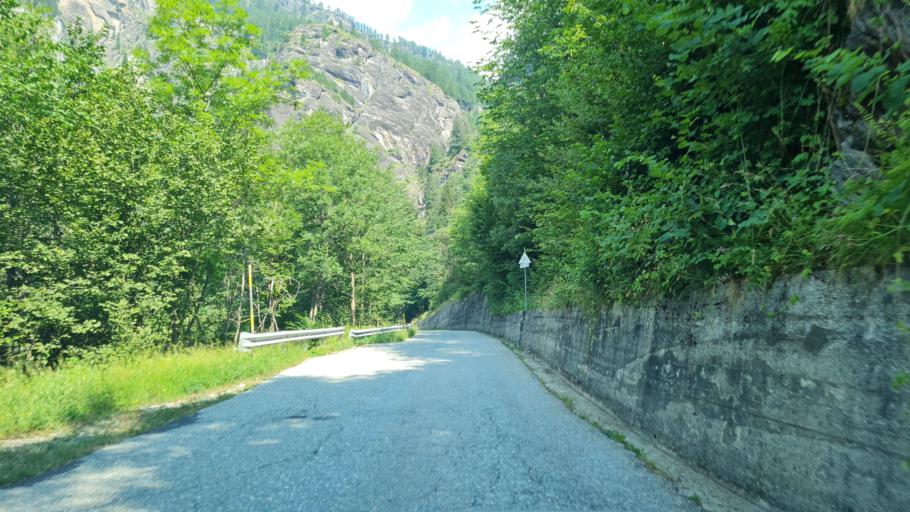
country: IT
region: Piedmont
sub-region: Provincia Verbano-Cusio-Ossola
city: Baceno
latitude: 46.2992
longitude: 8.2671
